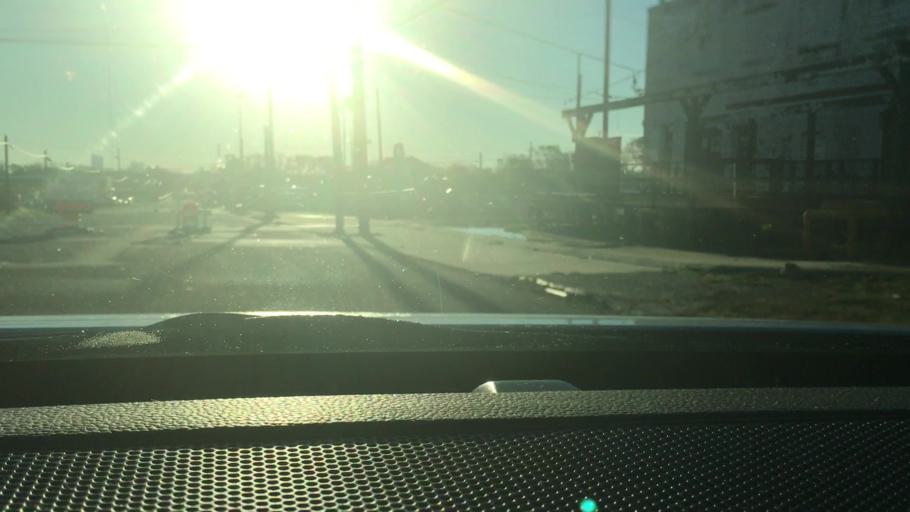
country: US
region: New Jersey
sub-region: Atlantic County
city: Pleasantville
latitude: 39.3927
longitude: -74.5202
